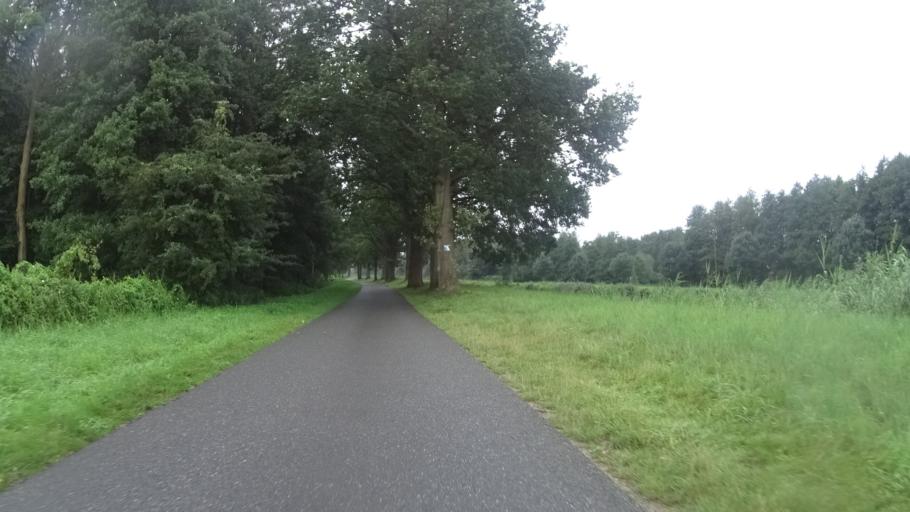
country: DE
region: Schleswig-Holstein
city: Dalldorf
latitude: 53.4332
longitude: 10.6150
